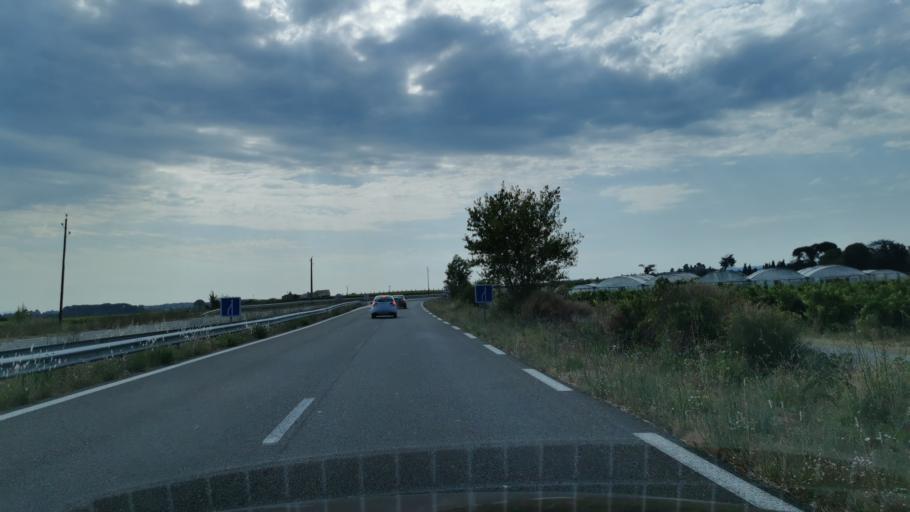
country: FR
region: Languedoc-Roussillon
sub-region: Departement de l'Herault
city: Puisserguier
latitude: 43.3654
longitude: 3.0737
